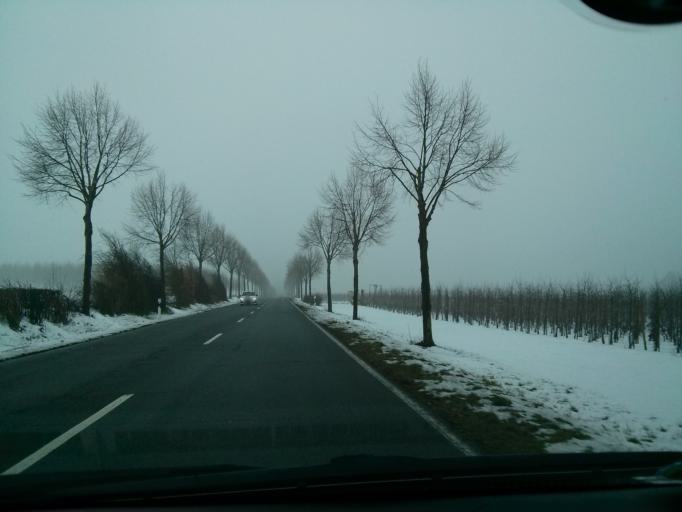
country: DE
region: North Rhine-Westphalia
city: Meckenheim
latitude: 50.6099
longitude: 7.0197
